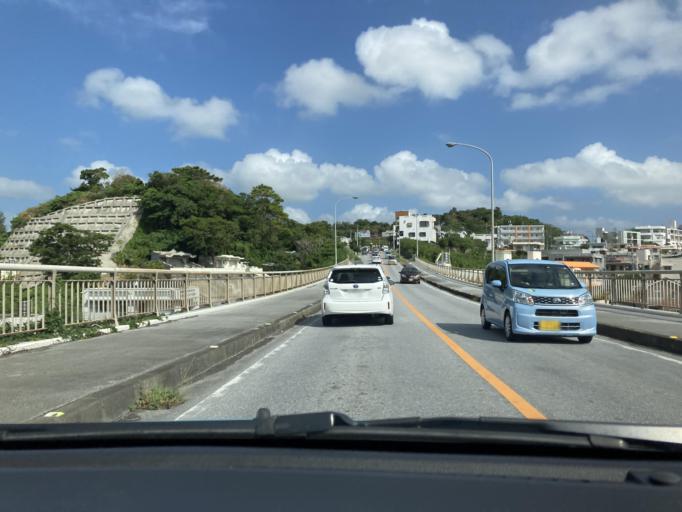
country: JP
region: Okinawa
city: Chatan
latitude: 26.2938
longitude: 127.7846
